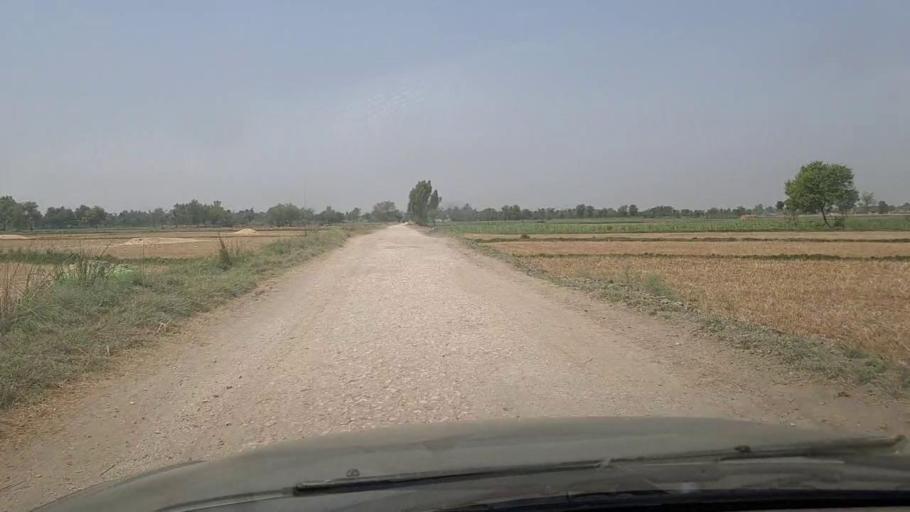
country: PK
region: Sindh
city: Adilpur
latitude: 27.9347
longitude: 69.2741
